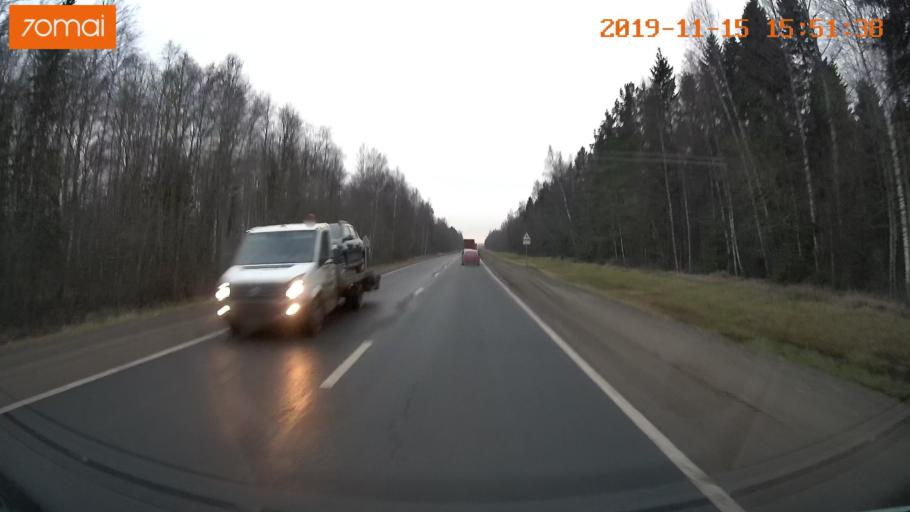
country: RU
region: Jaroslavl
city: Yaroslavl
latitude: 57.8921
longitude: 40.0060
